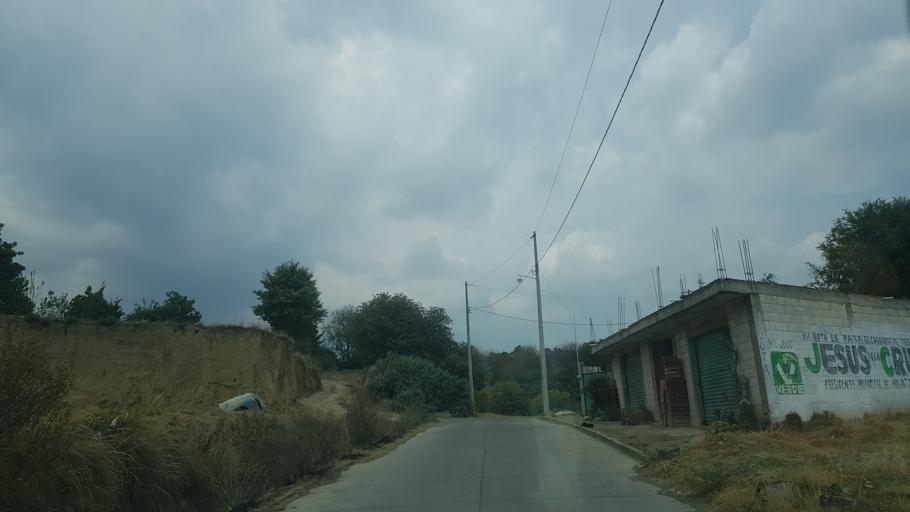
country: MX
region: Puebla
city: Domingo Arenas
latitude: 19.1409
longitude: -98.4775
